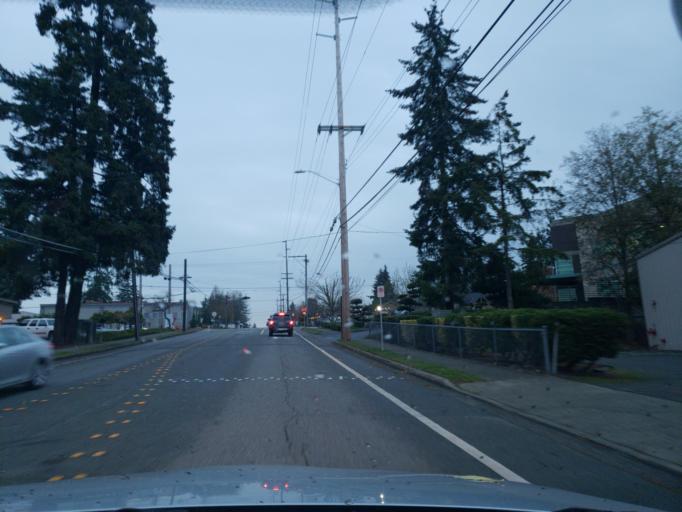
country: US
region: Washington
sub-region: Snohomish County
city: Lynnwood
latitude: 47.8068
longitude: -122.3208
